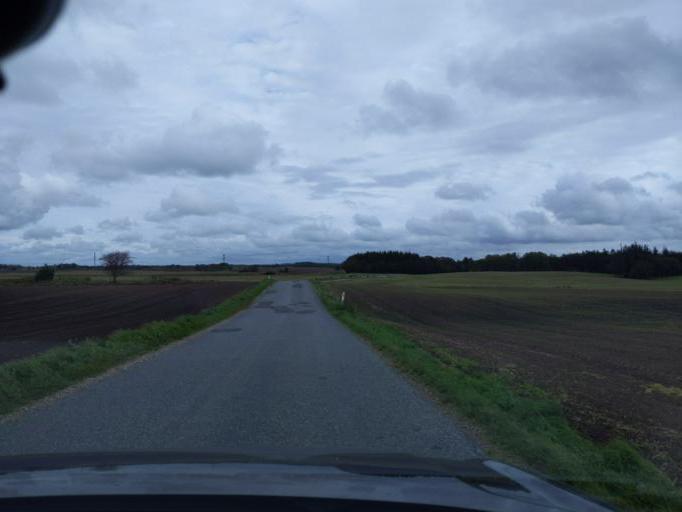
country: DK
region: Central Jutland
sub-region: Viborg Kommune
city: Bjerringbro
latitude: 56.4074
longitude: 9.5569
